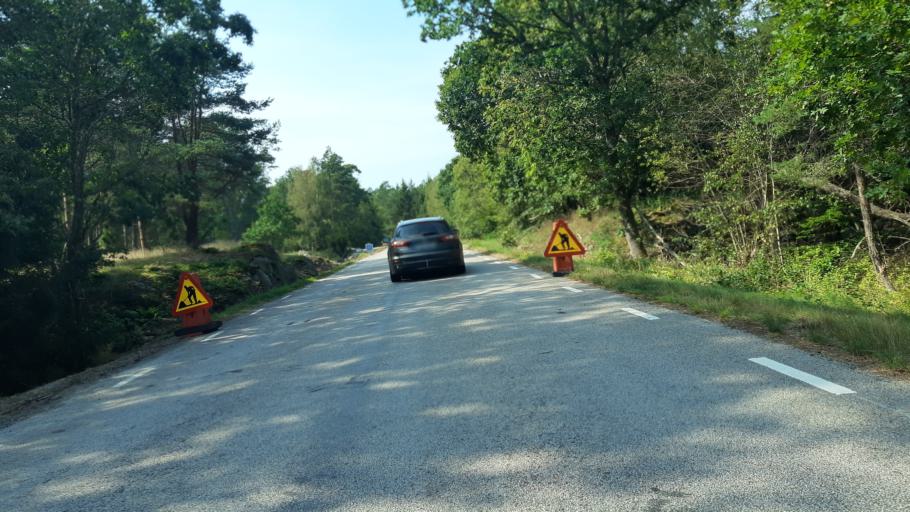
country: SE
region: Blekinge
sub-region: Ronneby Kommun
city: Brakne-Hoby
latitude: 56.1799
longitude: 15.1296
